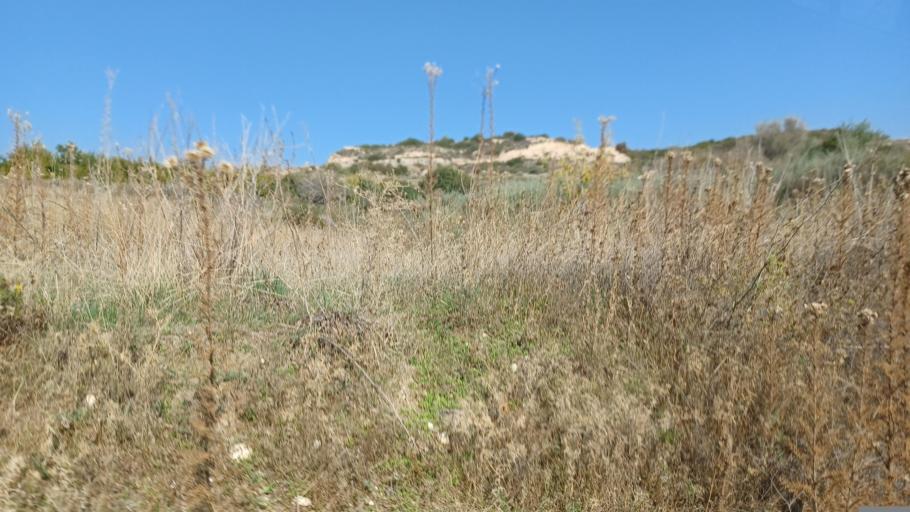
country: CY
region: Pafos
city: Kissonerga
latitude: 34.8460
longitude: 32.3945
